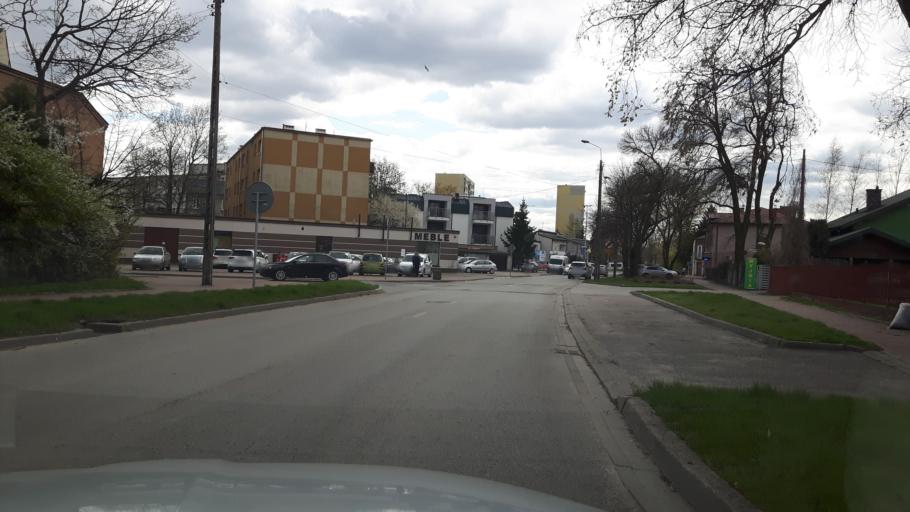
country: PL
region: Masovian Voivodeship
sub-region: Powiat wolominski
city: Wolomin
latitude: 52.3444
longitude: 21.2347
